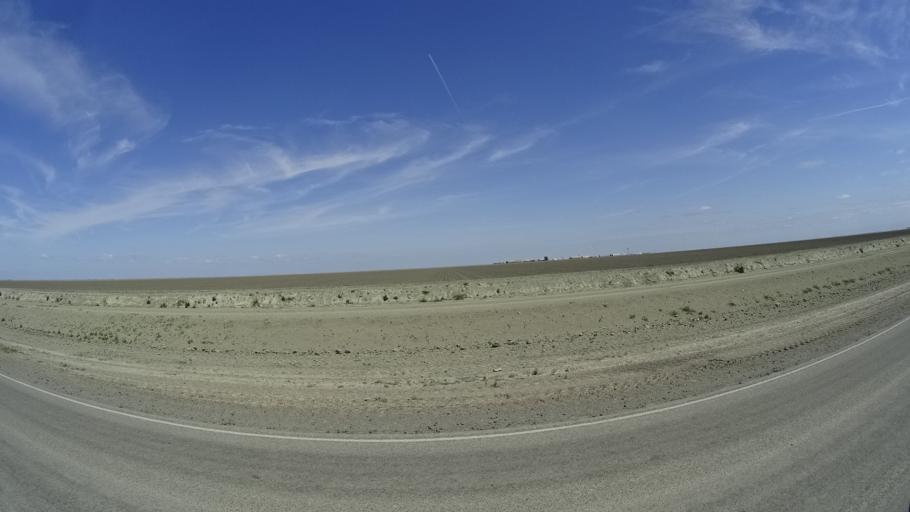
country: US
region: California
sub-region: Tulare County
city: Alpaugh
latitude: 35.9343
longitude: -119.5976
